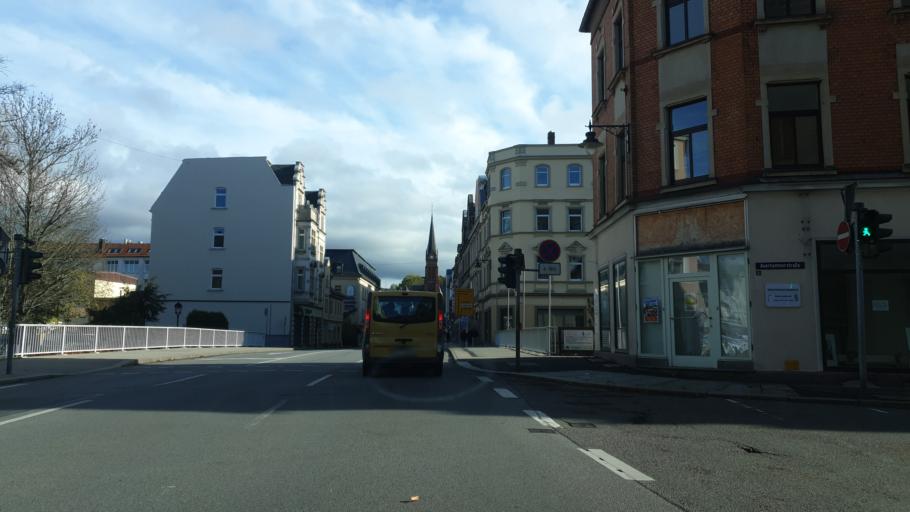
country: DE
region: Saxony
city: Aue
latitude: 50.5869
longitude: 12.6996
